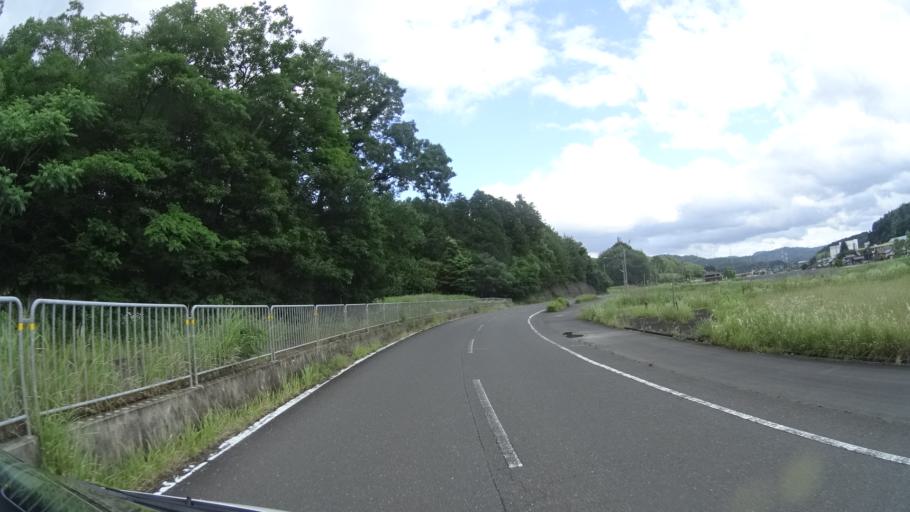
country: JP
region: Kyoto
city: Ayabe
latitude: 35.3387
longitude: 135.2934
